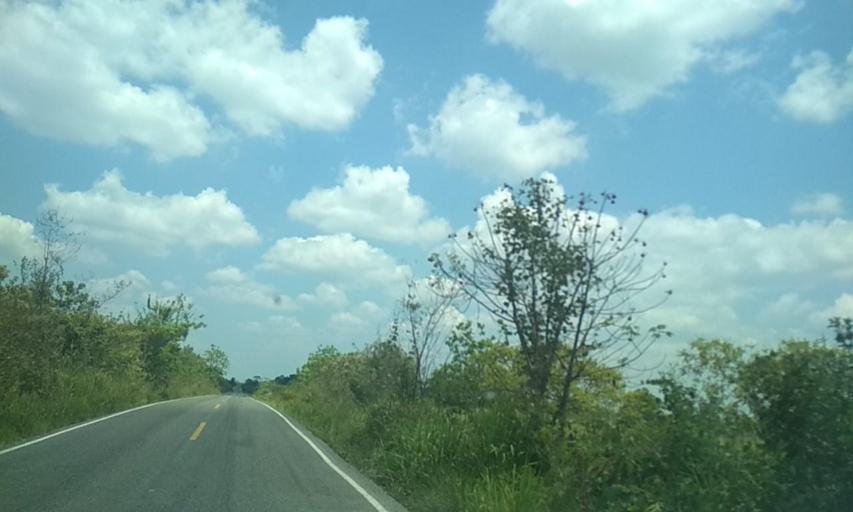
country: MX
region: Tabasco
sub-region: Huimanguillo
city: Huapacal 1ra. Seccion
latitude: 17.7535
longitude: -93.7422
